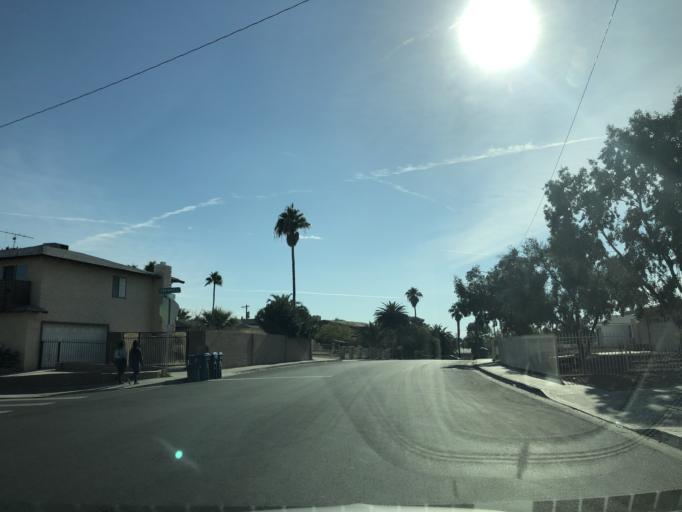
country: US
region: Nevada
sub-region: Clark County
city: Winchester
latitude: 36.1252
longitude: -115.1323
